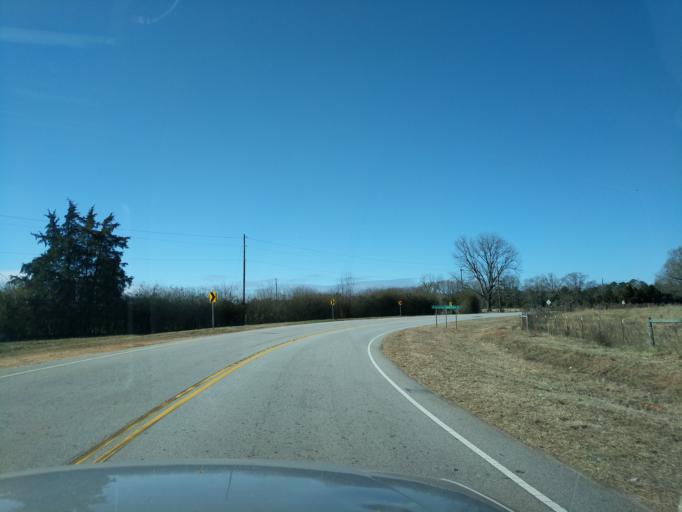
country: US
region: South Carolina
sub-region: Saluda County
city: Saluda
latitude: 34.0474
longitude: -81.8189
